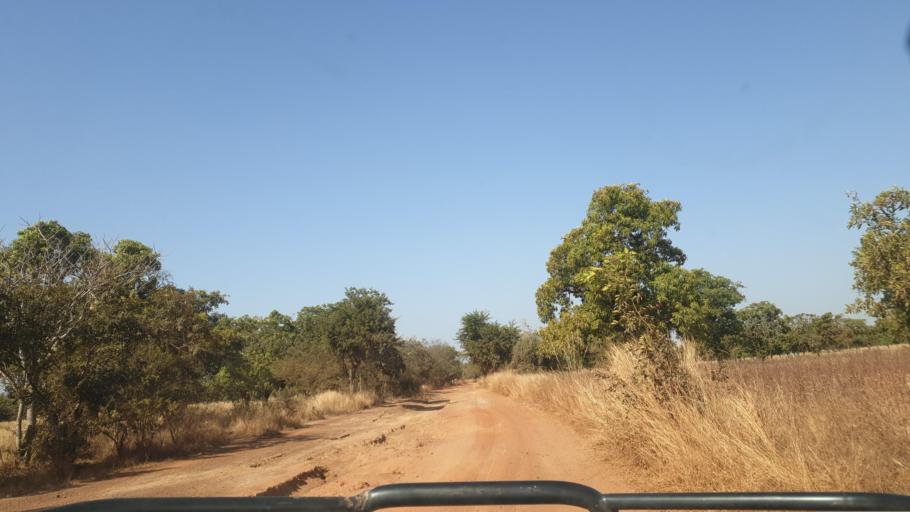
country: ML
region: Sikasso
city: Bougouni
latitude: 11.8210
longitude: -6.9658
